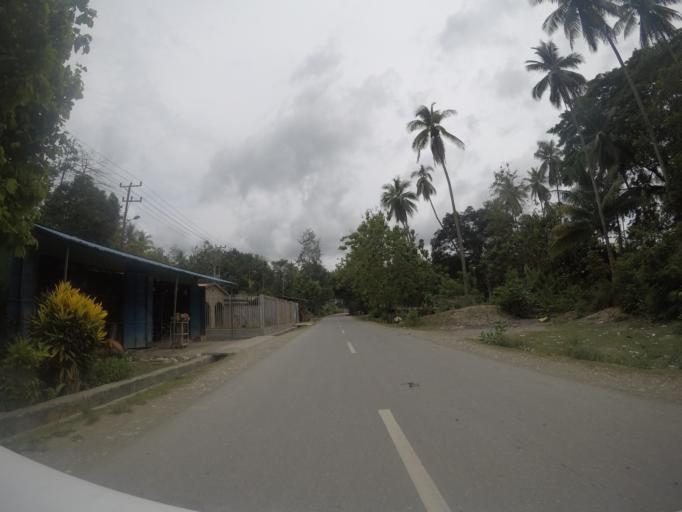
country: TL
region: Viqueque
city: Viqueque
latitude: -8.8689
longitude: 126.3716
